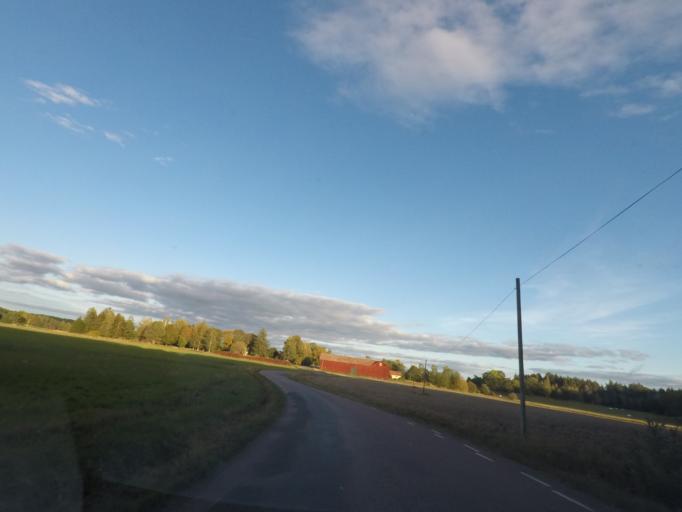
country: SE
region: Vaestmanland
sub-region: Kungsors Kommun
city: Kungsoer
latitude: 59.5078
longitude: 16.1034
